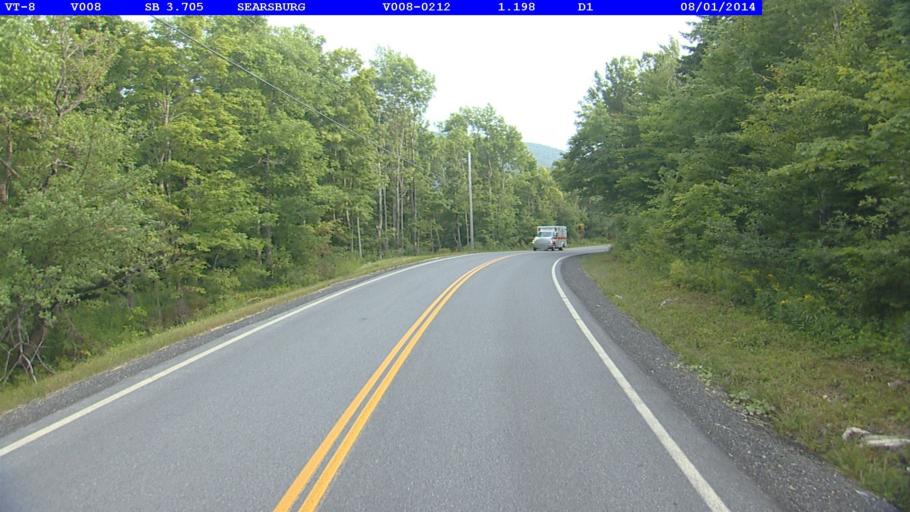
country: US
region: Vermont
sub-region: Windham County
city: Dover
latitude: 42.8744
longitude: -72.9692
